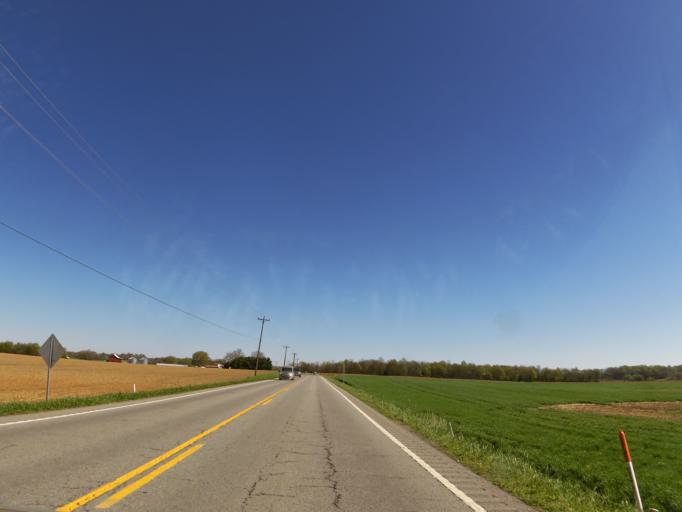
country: US
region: Tennessee
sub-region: Robertson County
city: Springfield
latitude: 36.5893
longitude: -86.8537
